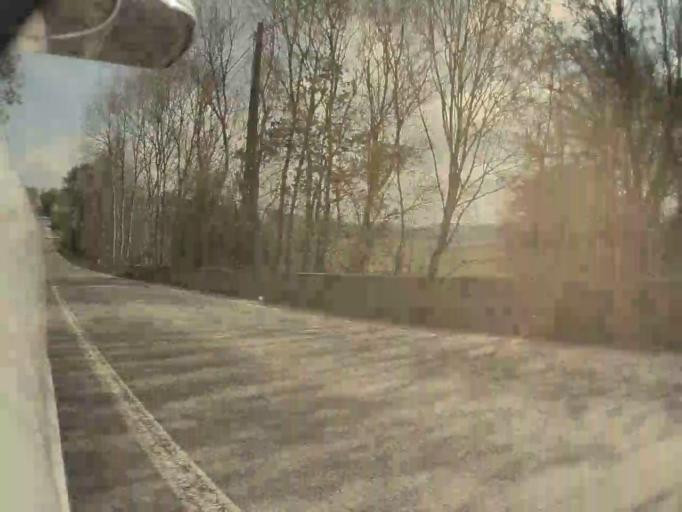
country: BE
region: Wallonia
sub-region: Province de Namur
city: Somme-Leuze
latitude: 50.3349
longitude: 5.3654
